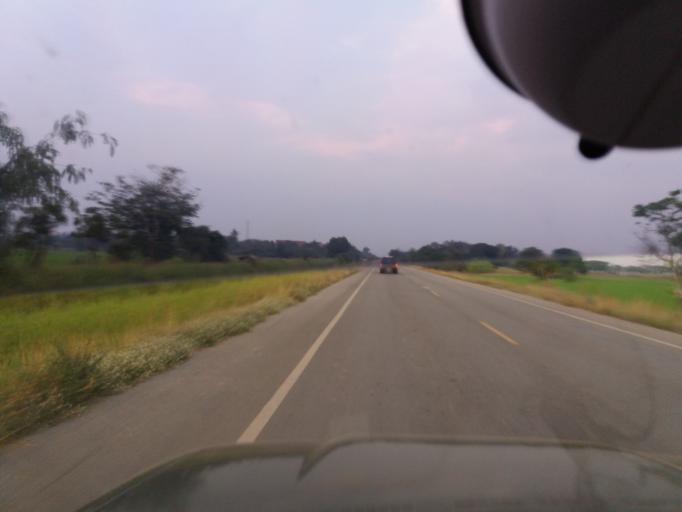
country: TH
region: Suphan Buri
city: Doem Bang Nang Buat
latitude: 14.8950
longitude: 100.1324
